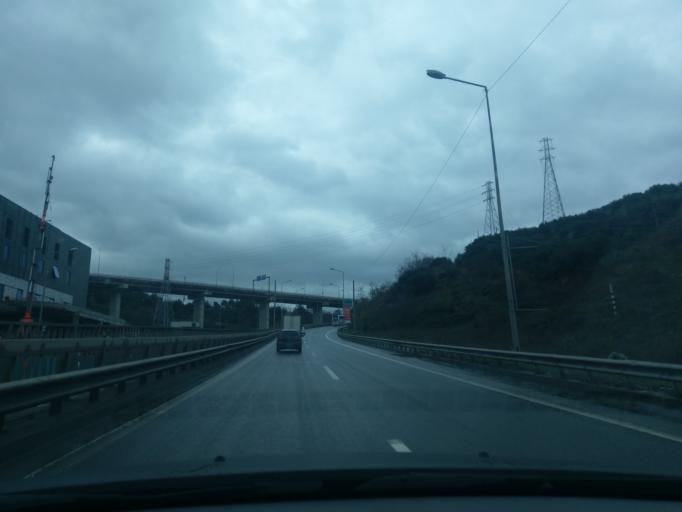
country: TR
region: Istanbul
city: Sisli
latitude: 41.0924
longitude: 28.9536
